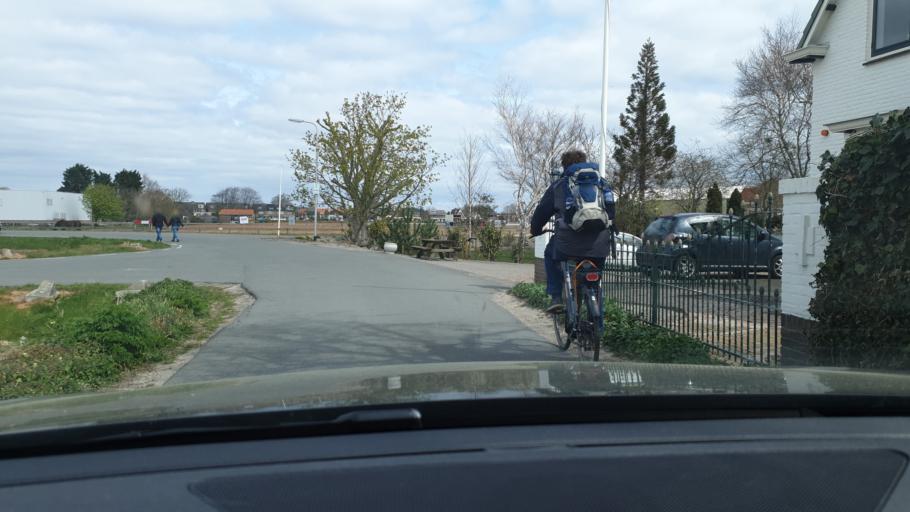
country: NL
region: South Holland
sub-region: Gemeente Lisse
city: Lisse
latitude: 52.2973
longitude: 4.5417
